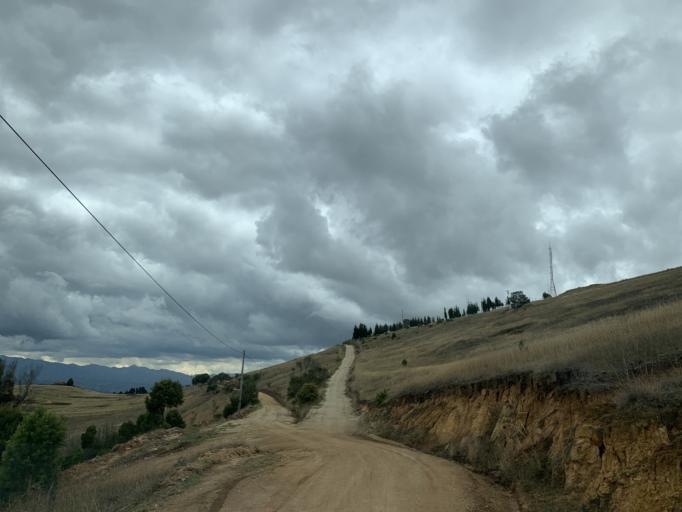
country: CO
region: Boyaca
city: Tunja
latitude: 5.5501
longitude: -73.3183
